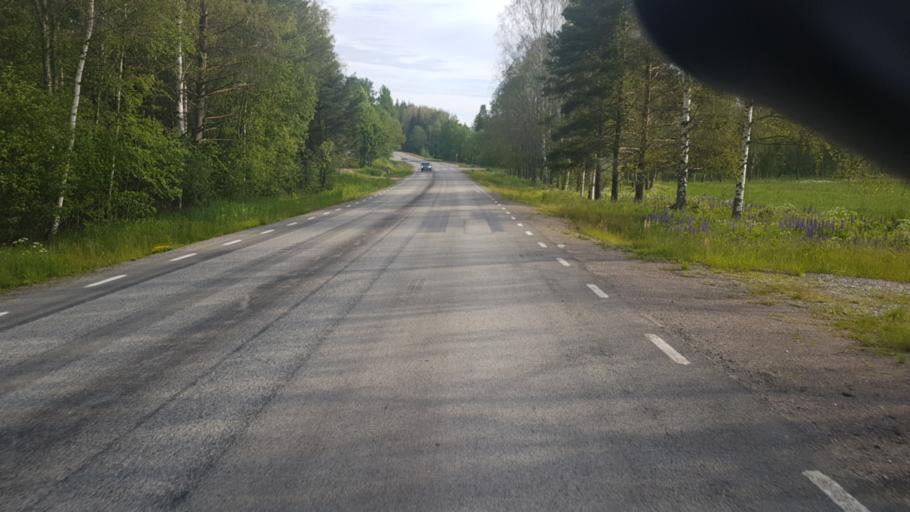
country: SE
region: Vaermland
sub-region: Arvika Kommun
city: Arvika
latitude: 59.6718
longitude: 12.6274
